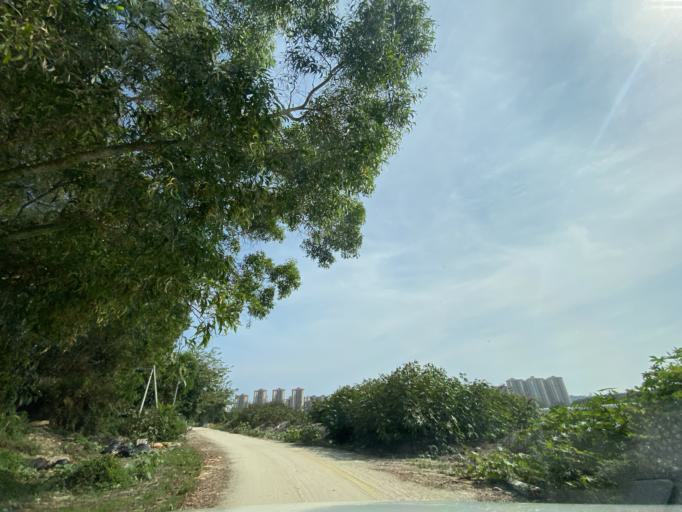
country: CN
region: Hainan
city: Yingzhou
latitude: 18.4076
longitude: 109.8357
